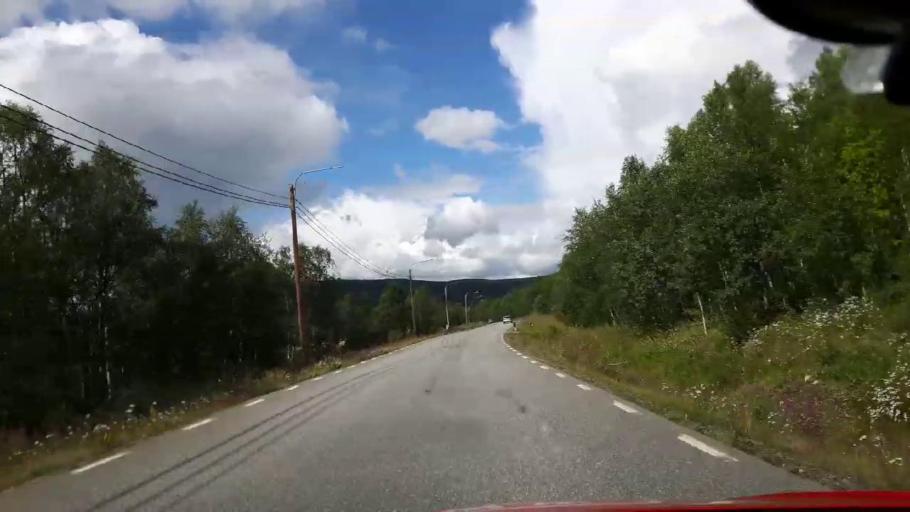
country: NO
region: Nordland
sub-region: Hattfjelldal
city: Hattfjelldal
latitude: 65.0638
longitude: 14.8542
